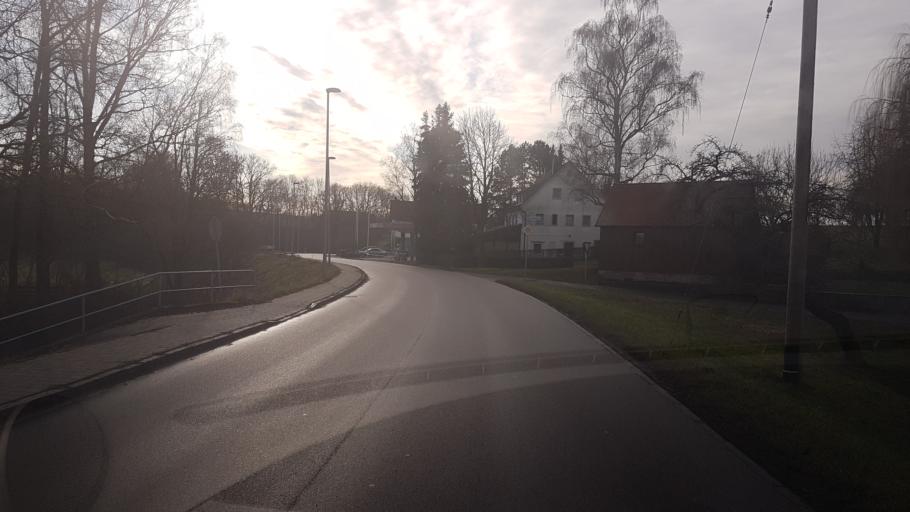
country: DE
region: Baden-Wuerttemberg
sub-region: Regierungsbezirk Stuttgart
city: Kirchberg an der Jagst
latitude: 49.2179
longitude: 10.0053
